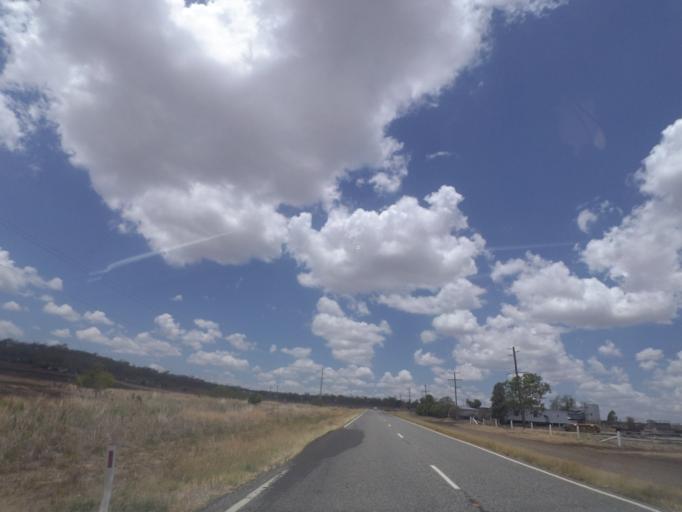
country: AU
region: Queensland
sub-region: Toowoomba
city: Top Camp
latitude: -27.8765
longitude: 151.9665
